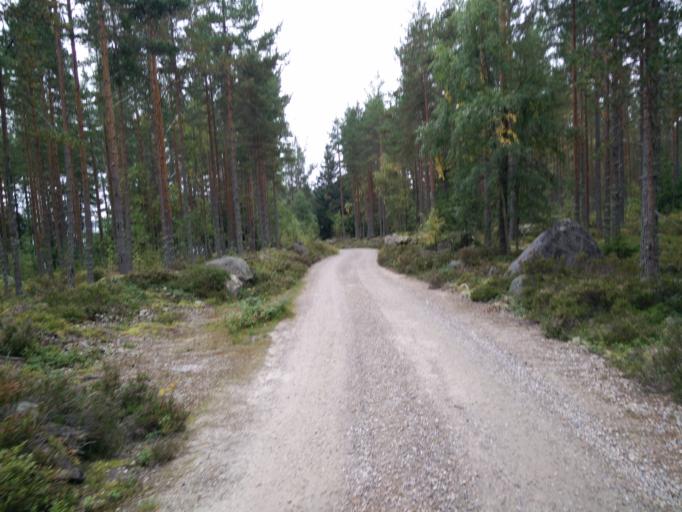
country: SE
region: Gaevleborg
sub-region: Hudiksvalls Kommun
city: Hudiksvall
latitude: 61.8342
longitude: 17.3389
